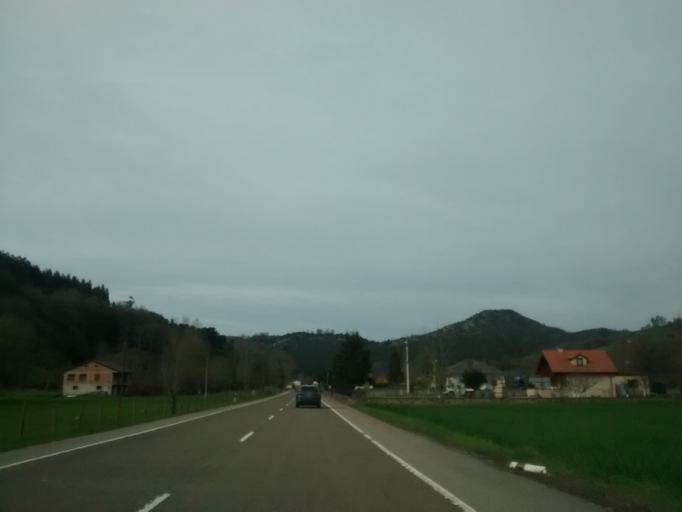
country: ES
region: Cantabria
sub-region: Provincia de Cantabria
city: Corvera
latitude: 43.2698
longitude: -3.9471
